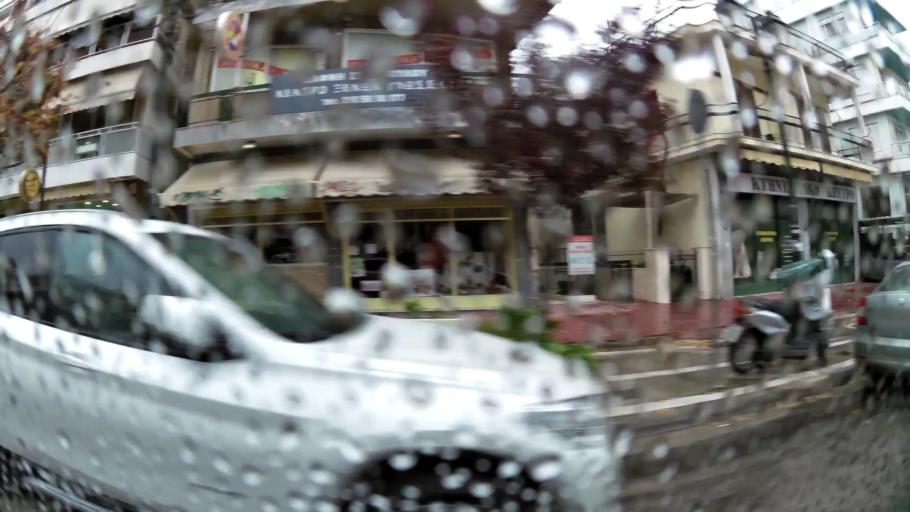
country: GR
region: Attica
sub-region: Nomarchia Athinas
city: Chaidari
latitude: 38.0062
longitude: 23.6603
